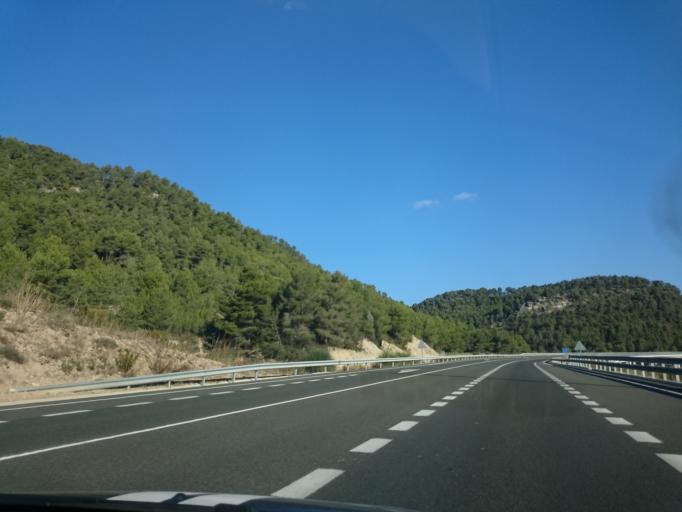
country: ES
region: Catalonia
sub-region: Provincia de Barcelona
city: Castelloli
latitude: 41.6057
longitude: 1.6761
